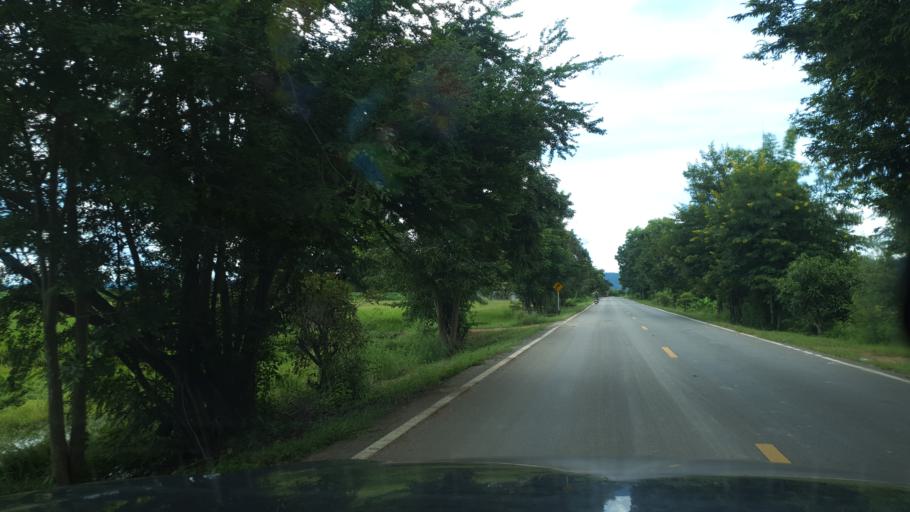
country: TH
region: Sukhothai
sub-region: Amphoe Si Satchanalai
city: Si Satchanalai
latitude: 17.4639
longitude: 99.7599
